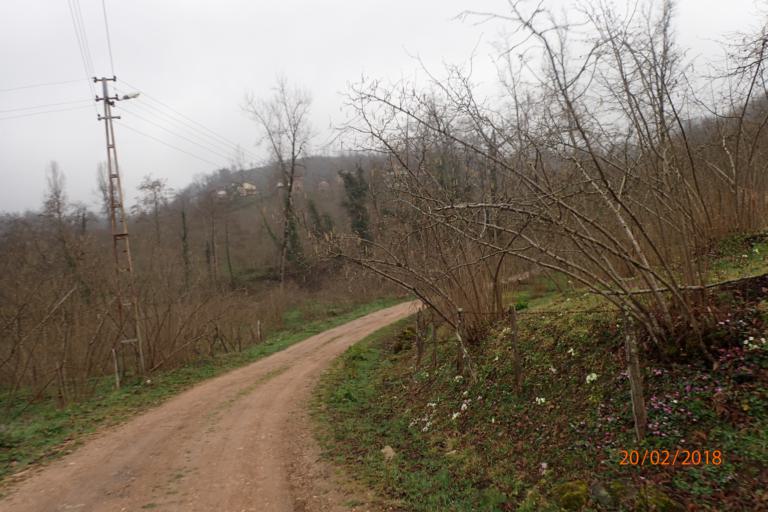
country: TR
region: Ordu
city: Camas
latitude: 40.9443
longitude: 37.5370
